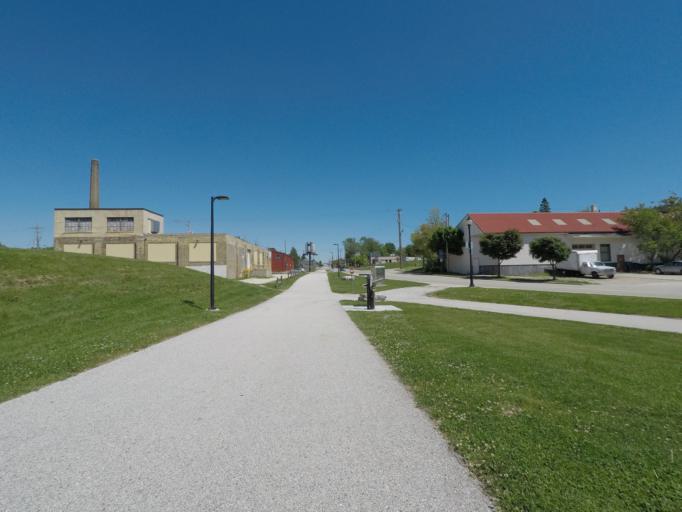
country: US
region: Wisconsin
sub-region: Sheboygan County
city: Sheboygan
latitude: 43.7556
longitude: -87.7214
